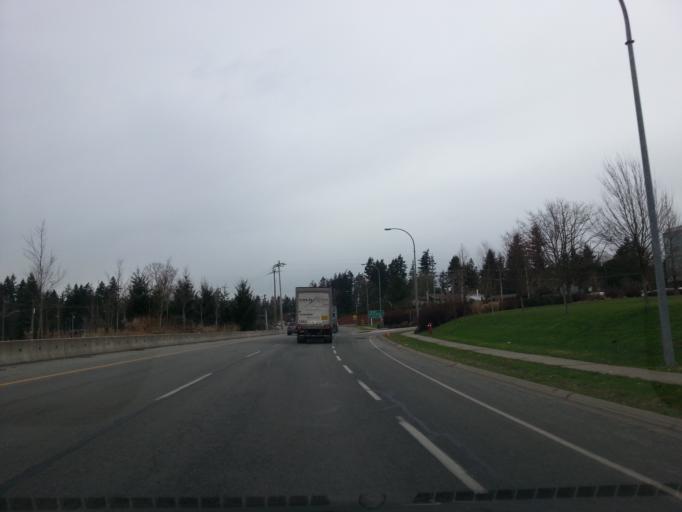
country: CA
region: British Columbia
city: Surrey
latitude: 49.1047
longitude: -122.8278
